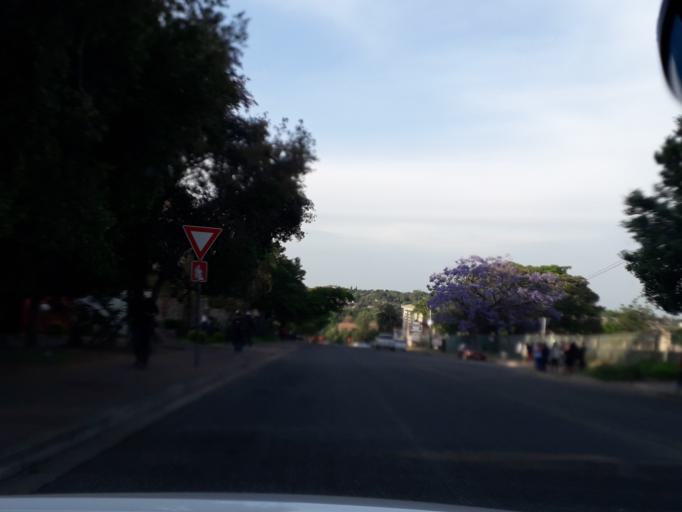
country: ZA
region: Gauteng
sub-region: City of Johannesburg Metropolitan Municipality
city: Johannesburg
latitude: -26.0918
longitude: 28.0006
